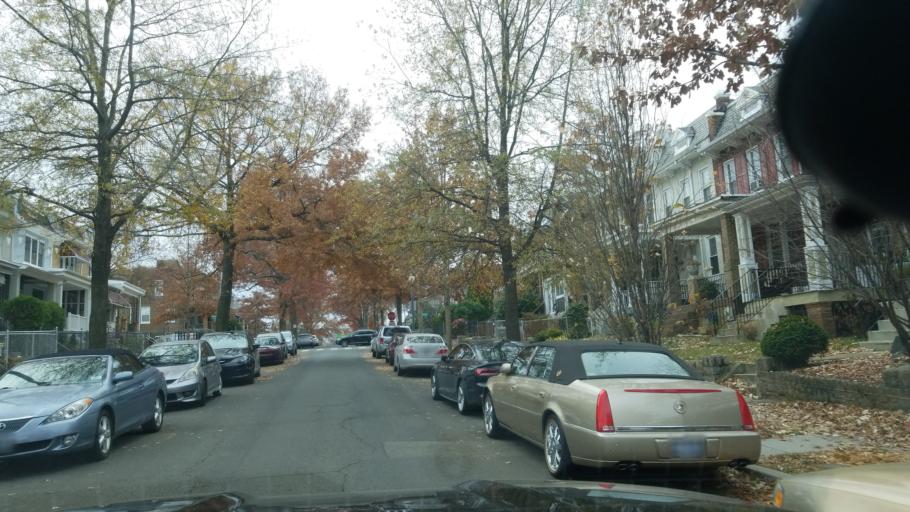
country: US
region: Maryland
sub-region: Prince George's County
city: Chillum
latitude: 38.9439
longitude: -77.0155
